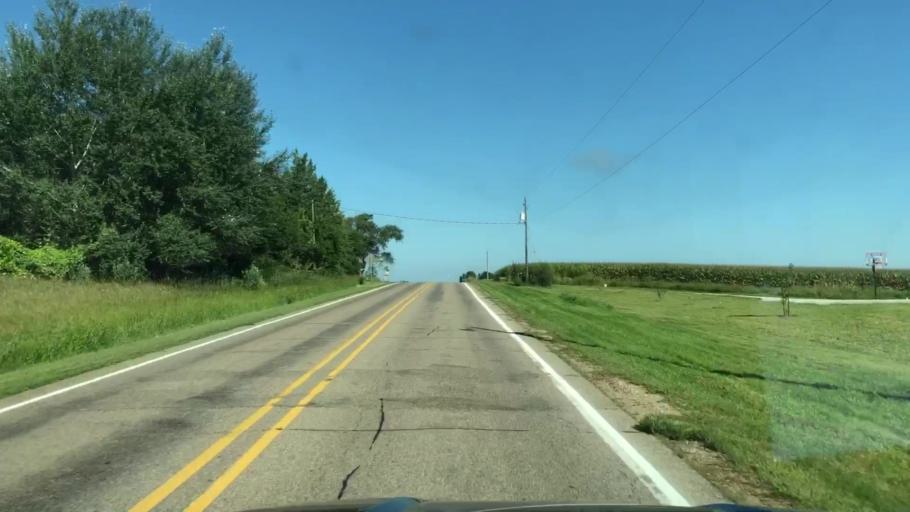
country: US
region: Iowa
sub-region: Woodbury County
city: Sergeant Bluff
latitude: 42.4259
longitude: -96.2783
